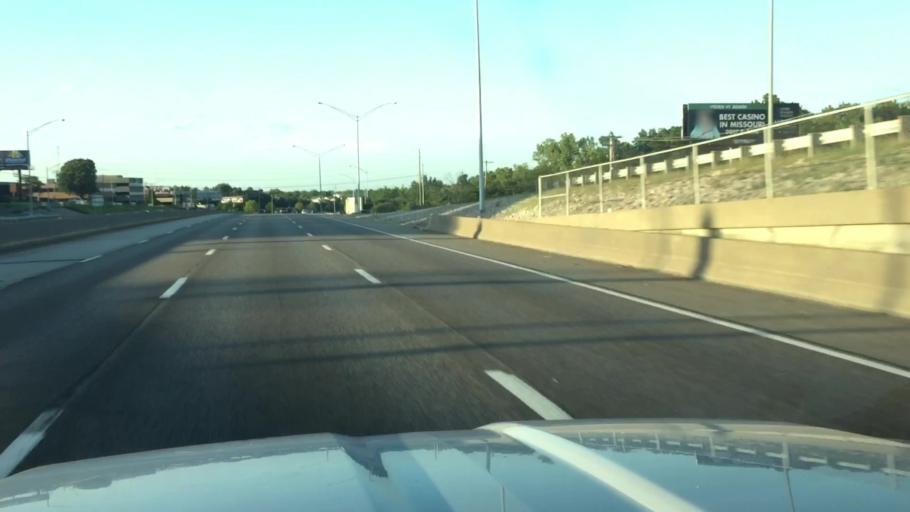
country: US
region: Missouri
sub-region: Saint Louis County
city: Green Park
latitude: 38.5126
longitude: -90.3353
